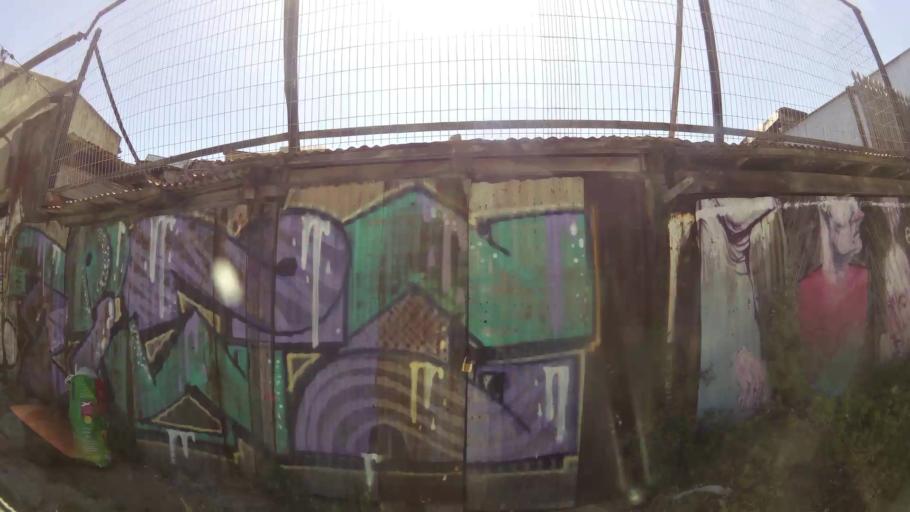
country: CL
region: Valparaiso
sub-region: Provincia de Valparaiso
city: Valparaiso
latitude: -33.0510
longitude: -71.5987
